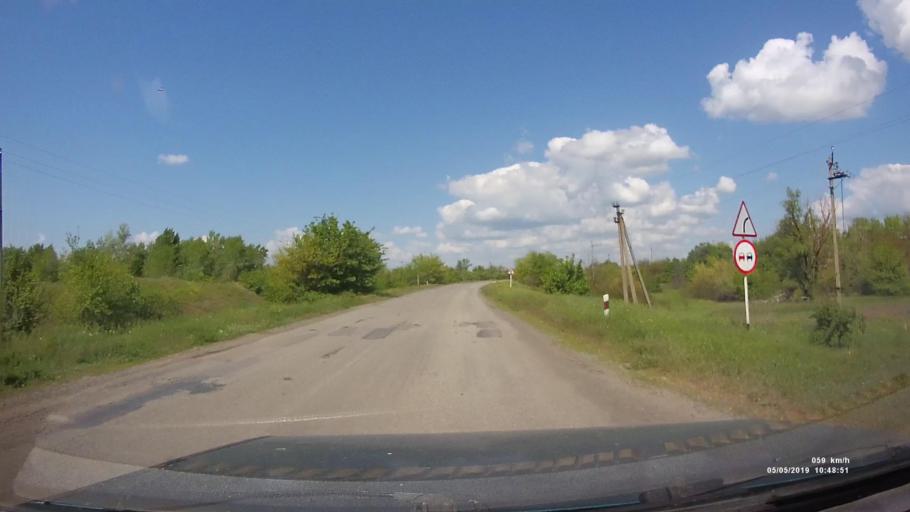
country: RU
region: Rostov
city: Ust'-Donetskiy
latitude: 47.6446
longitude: 40.8137
